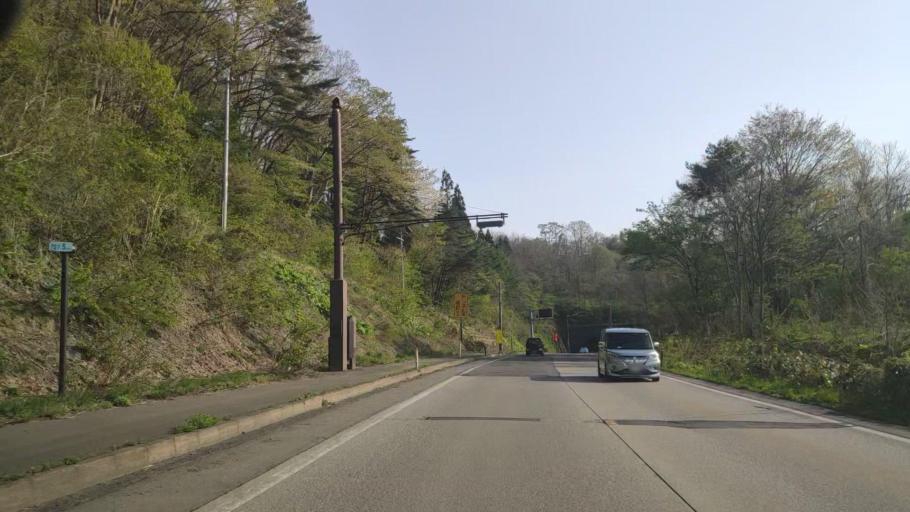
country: JP
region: Aomori
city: Aomori Shi
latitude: 40.8626
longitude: 140.8450
